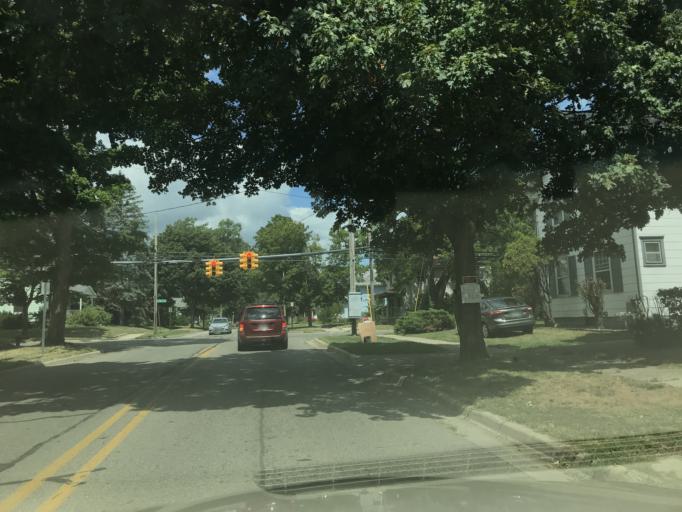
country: US
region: Michigan
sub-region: Jackson County
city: Jackson
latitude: 42.2397
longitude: -84.4185
